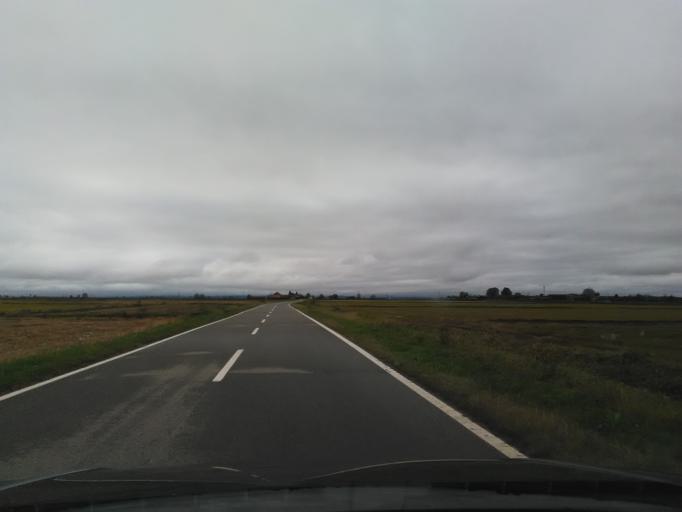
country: IT
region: Piedmont
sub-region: Provincia di Vercelli
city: Olcenengo
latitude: 45.3532
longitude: 8.3011
